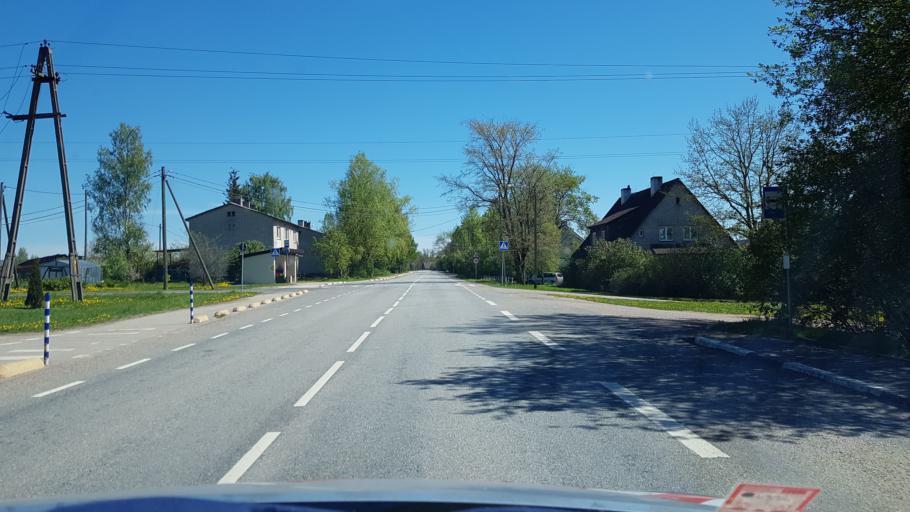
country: EE
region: Tartu
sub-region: UElenurme vald
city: Ulenurme
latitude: 58.2994
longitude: 26.8680
